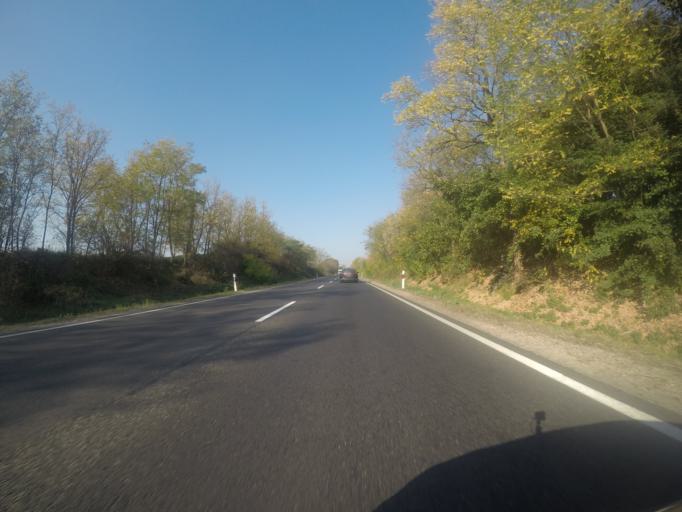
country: HU
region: Fejer
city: Baracs
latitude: 46.8687
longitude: 18.9192
